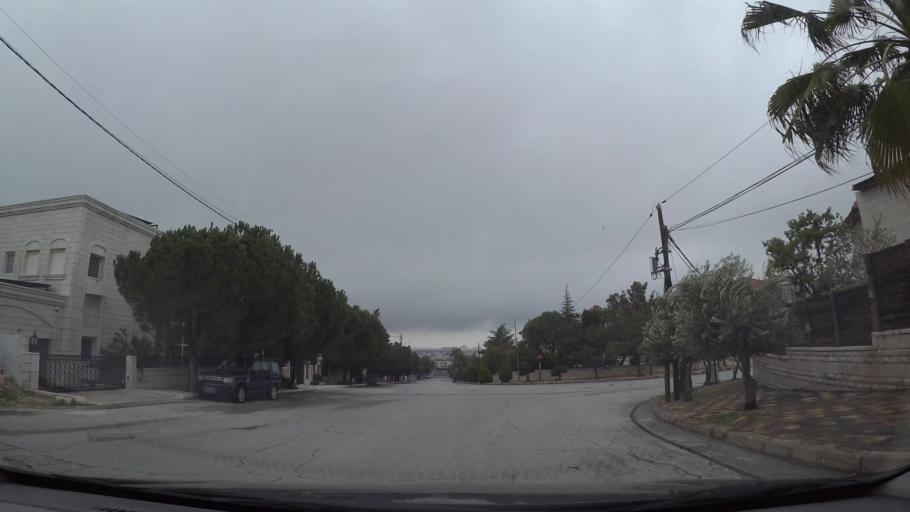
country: JO
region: Amman
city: Al Bunayyat ash Shamaliyah
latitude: 31.9378
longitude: 35.8821
